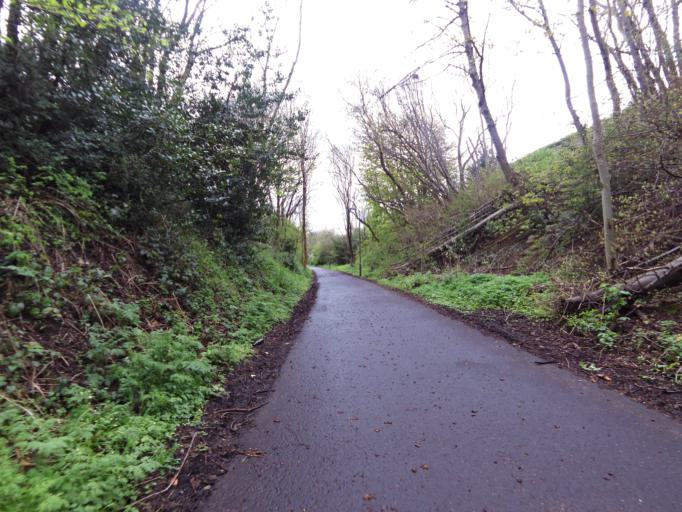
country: GB
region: Scotland
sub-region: Edinburgh
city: Edinburgh
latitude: 55.9551
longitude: -3.2432
